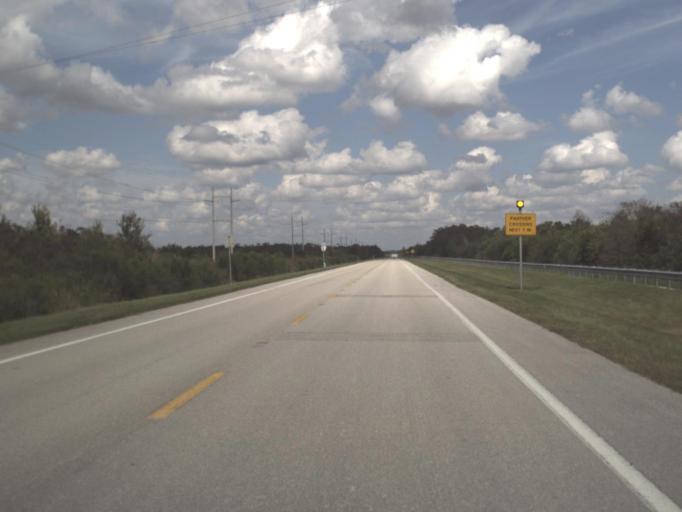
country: US
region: Florida
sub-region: Collier County
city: Lely Resort
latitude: 25.9649
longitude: -81.3535
